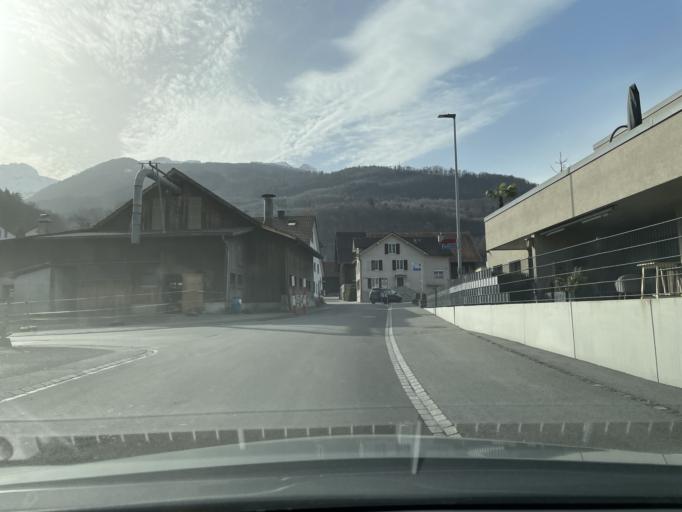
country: CH
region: Saint Gallen
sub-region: Wahlkreis Werdenberg
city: Buchs
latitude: 47.1591
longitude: 9.4738
